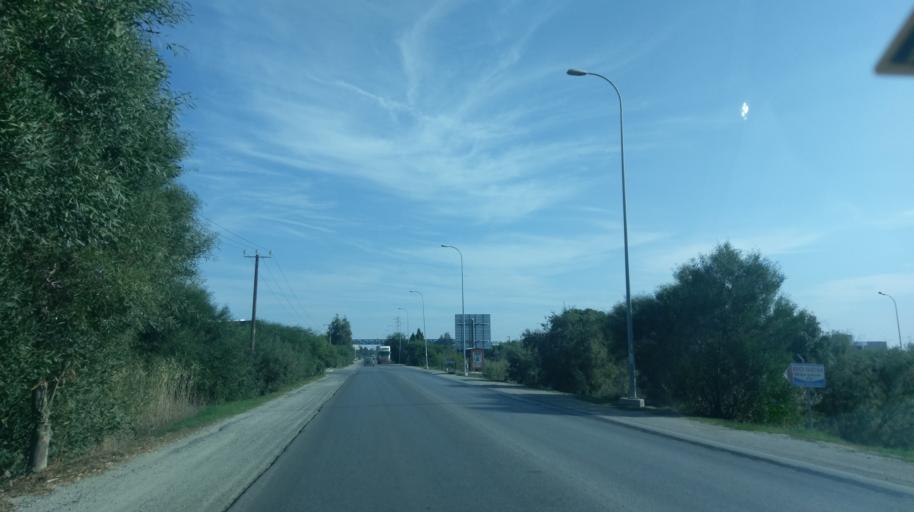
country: CY
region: Ammochostos
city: Famagusta
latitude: 35.1438
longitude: 33.8976
